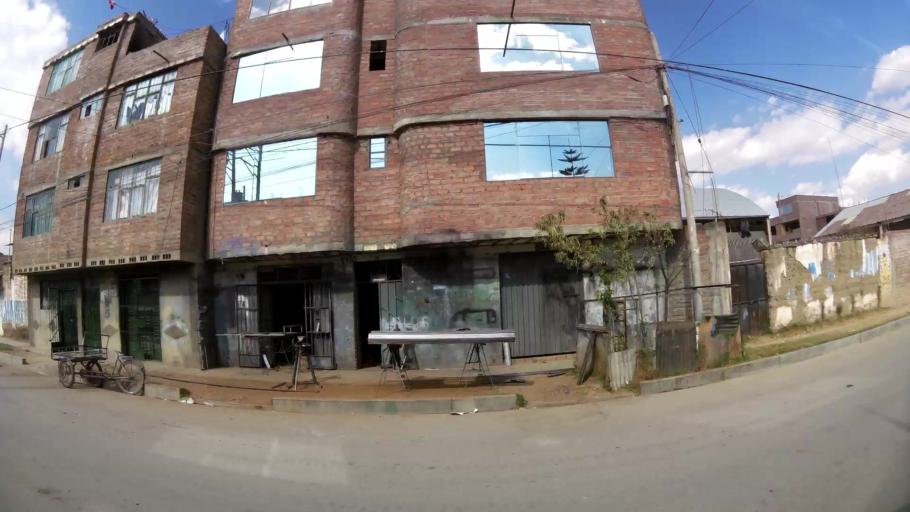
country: PE
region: Junin
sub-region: Provincia de Huancayo
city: El Tambo
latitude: -12.0775
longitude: -75.2149
